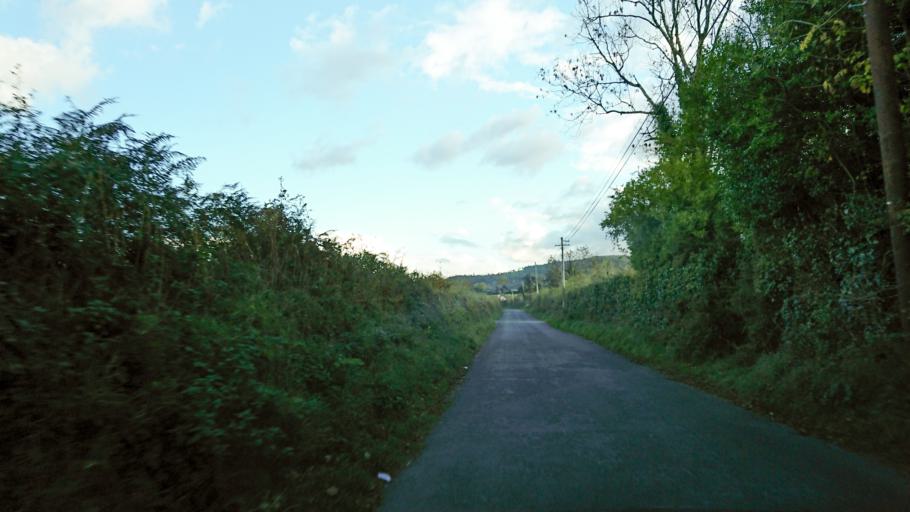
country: IE
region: Leinster
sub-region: Kilkenny
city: Graiguenamanagh
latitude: 52.4767
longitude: -6.9128
